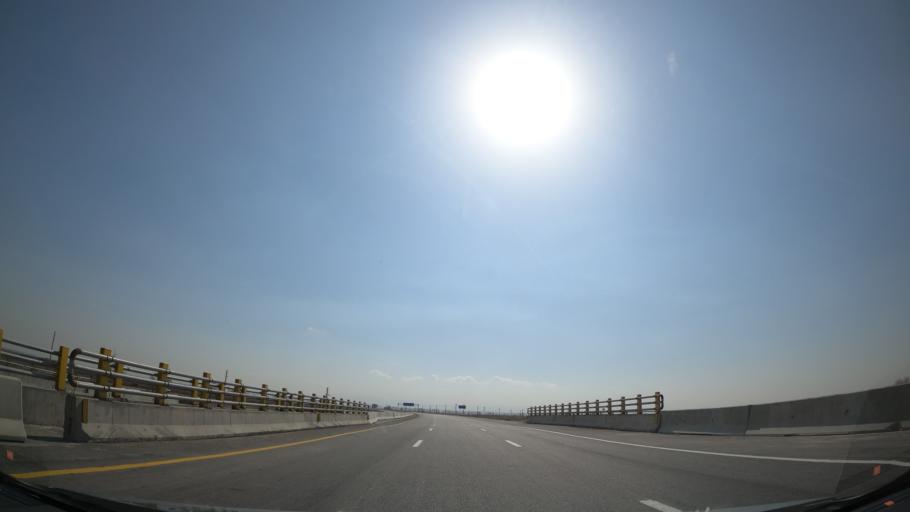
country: IR
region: Qazvin
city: Abyek
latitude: 35.9710
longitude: 50.4612
